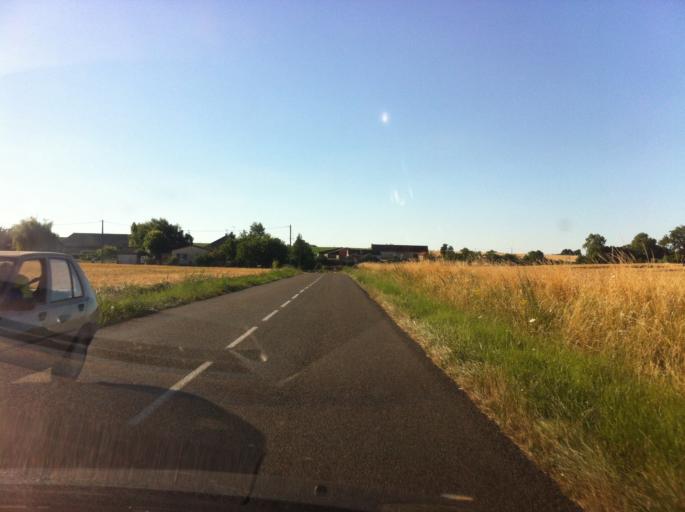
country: FR
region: Auvergne
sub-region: Departement de l'Allier
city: Chantelle
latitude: 46.2121
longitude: 3.1628
